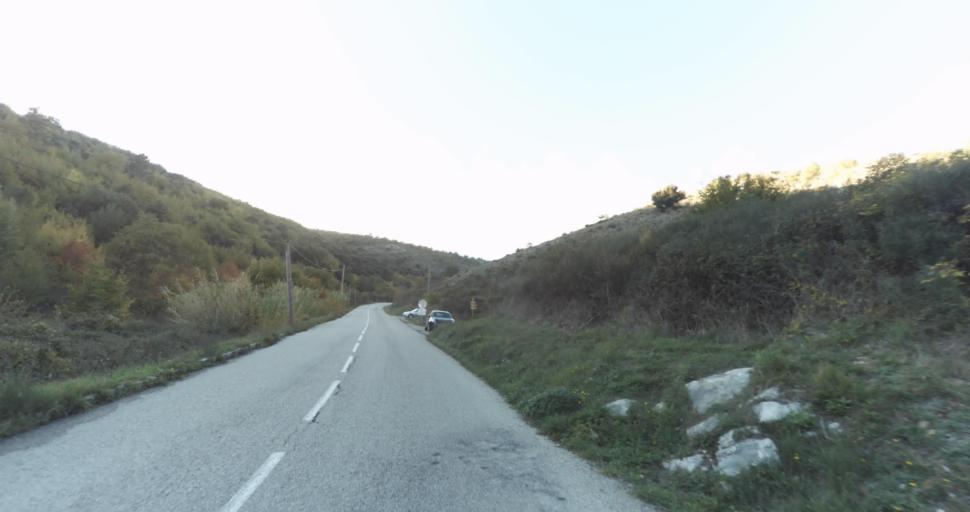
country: FR
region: Provence-Alpes-Cote d'Azur
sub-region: Departement des Alpes-Maritimes
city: Vence
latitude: 43.7464
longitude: 7.1009
